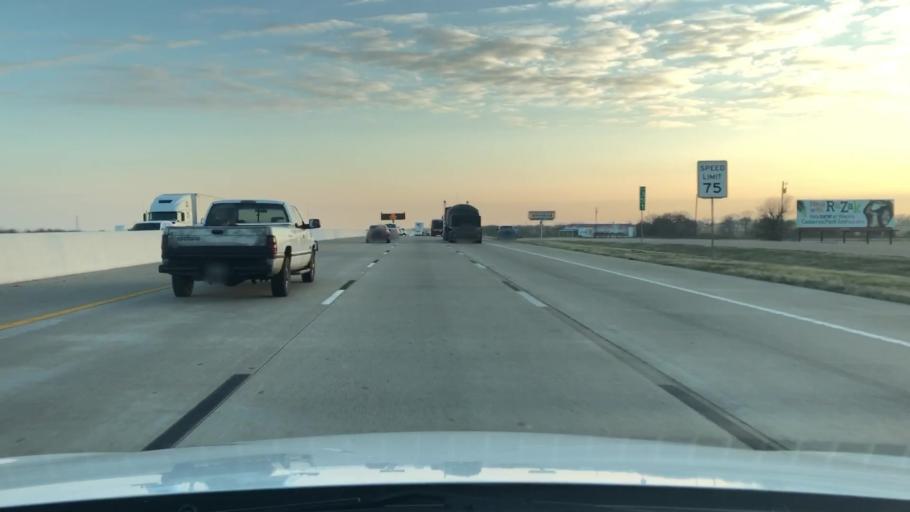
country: US
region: Texas
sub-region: McLennan County
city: West
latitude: 31.7750
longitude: -97.1044
